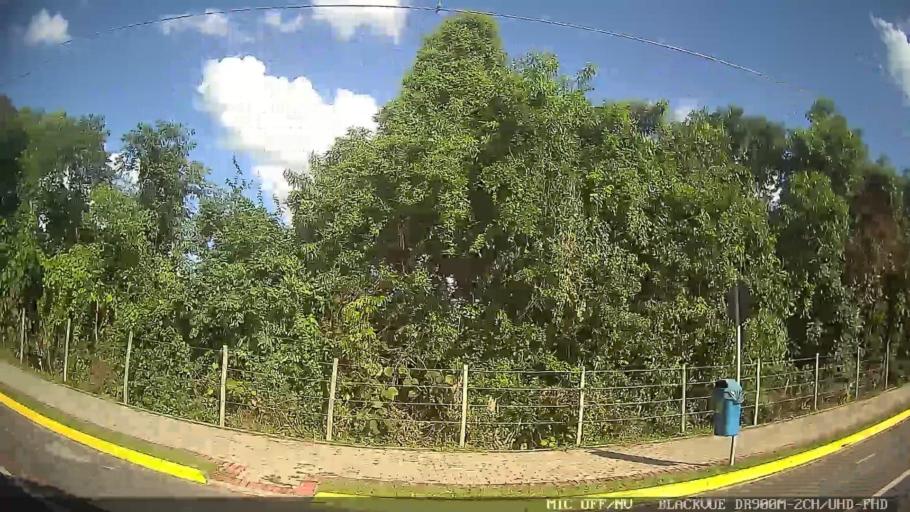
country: BR
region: Minas Gerais
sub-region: Extrema
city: Extrema
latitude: -22.8447
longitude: -46.3234
